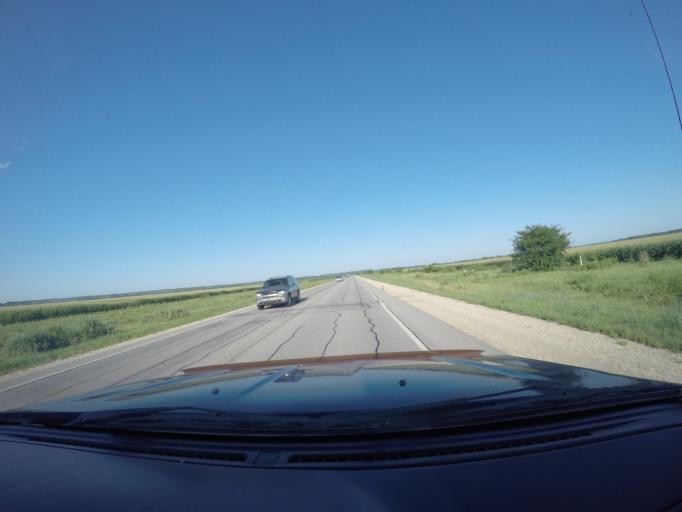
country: US
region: Kansas
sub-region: Jefferson County
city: Oskaloosa
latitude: 39.0872
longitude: -95.4454
